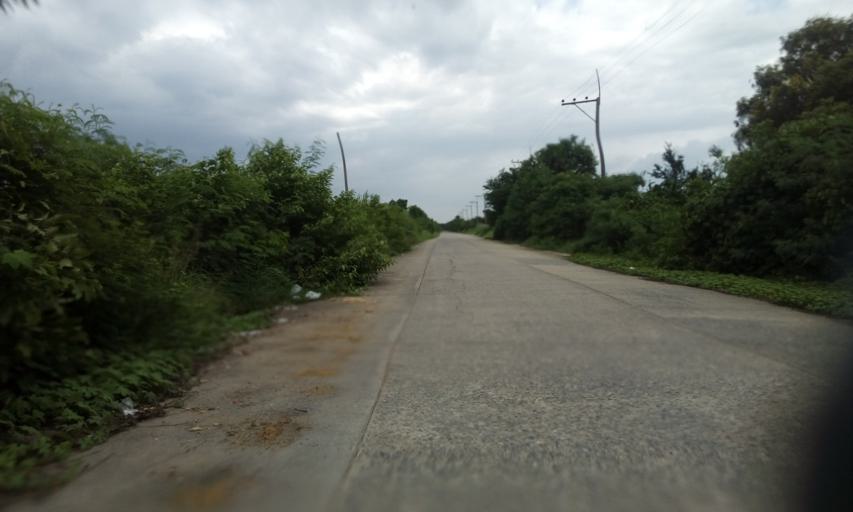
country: TH
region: Pathum Thani
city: Nong Suea
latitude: 14.0614
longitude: 100.8354
